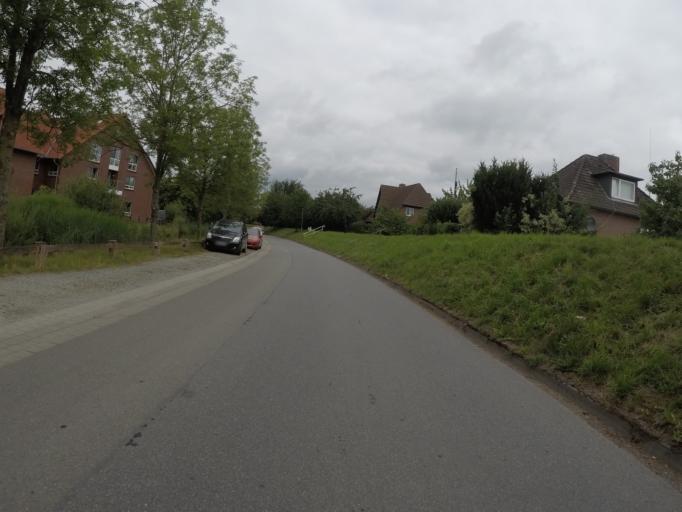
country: DE
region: Lower Saxony
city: Guderhandviertel
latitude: 53.5490
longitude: 9.6100
